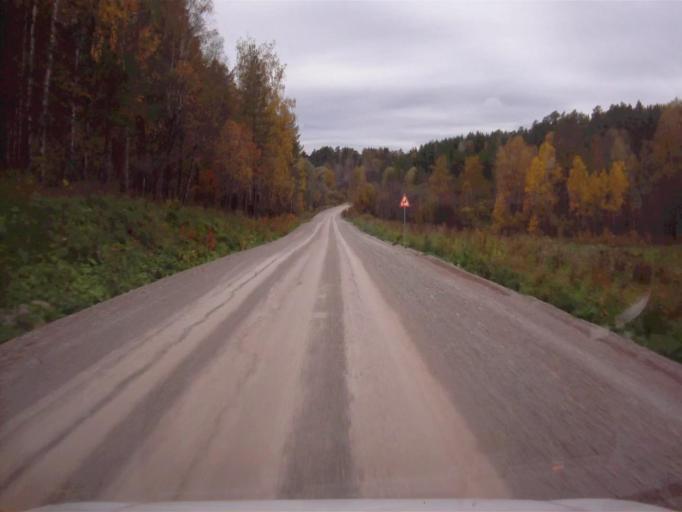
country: RU
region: Chelyabinsk
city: Nyazepetrovsk
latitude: 56.0570
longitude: 59.4638
